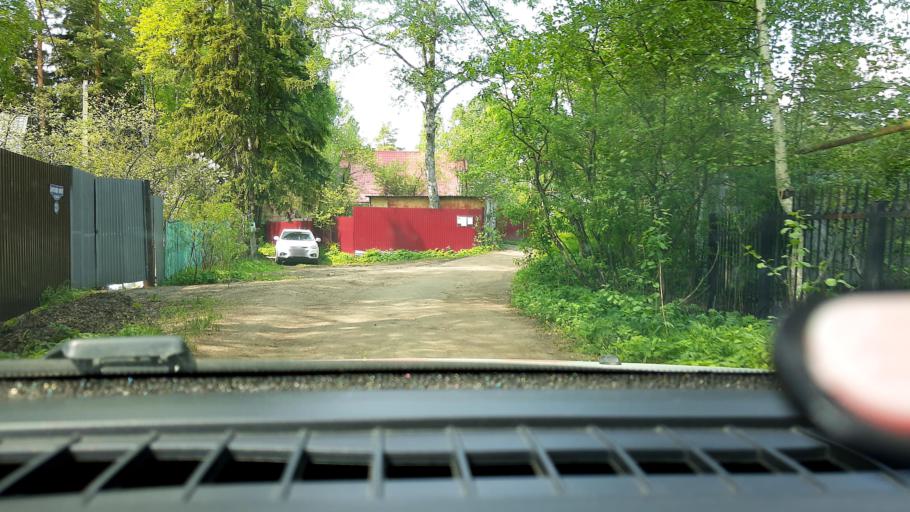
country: RU
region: Nizjnij Novgorod
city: Afonino
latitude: 56.1866
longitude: 44.1002
